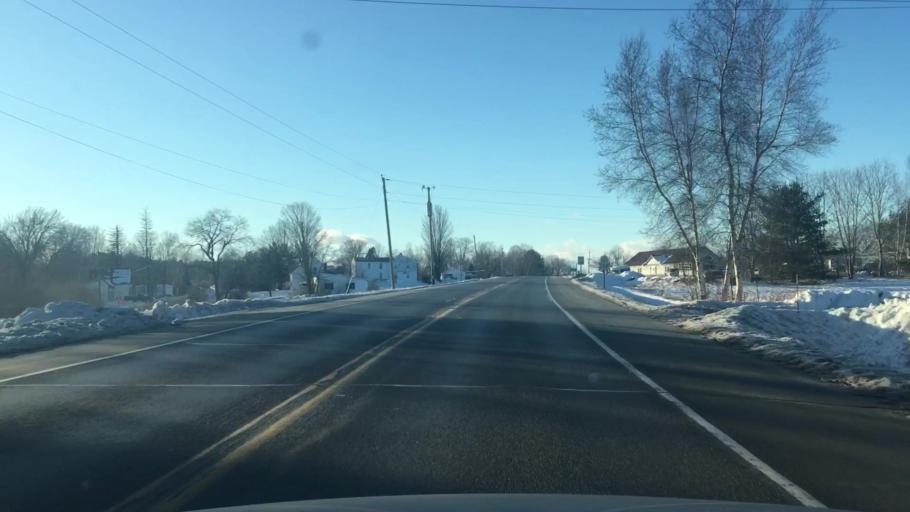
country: US
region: Maine
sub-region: Franklin County
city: New Sharon
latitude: 44.6364
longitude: -70.0078
